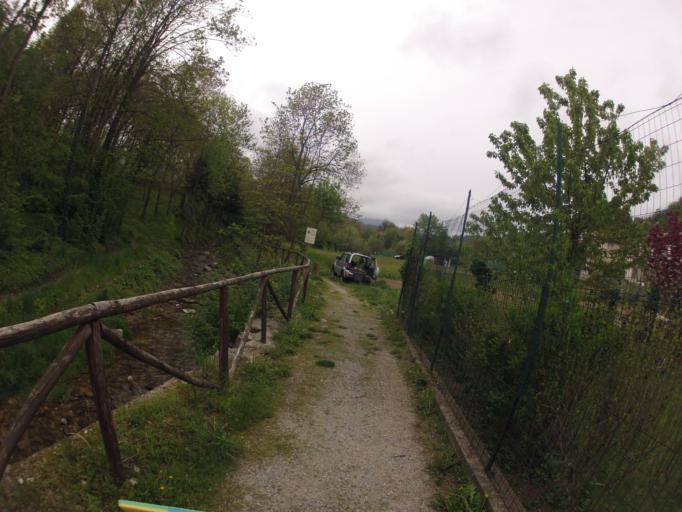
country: IT
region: Piedmont
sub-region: Provincia di Cuneo
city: Peveragno
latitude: 44.3294
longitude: 7.6108
